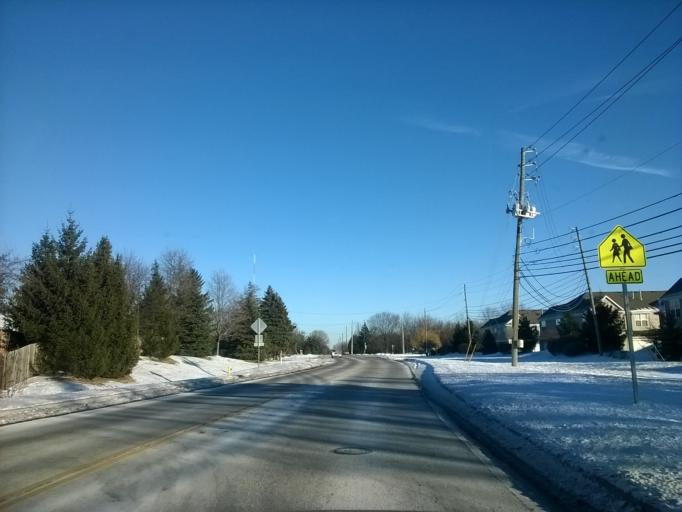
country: US
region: Indiana
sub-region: Marion County
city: Meridian Hills
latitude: 39.9267
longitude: -86.2010
